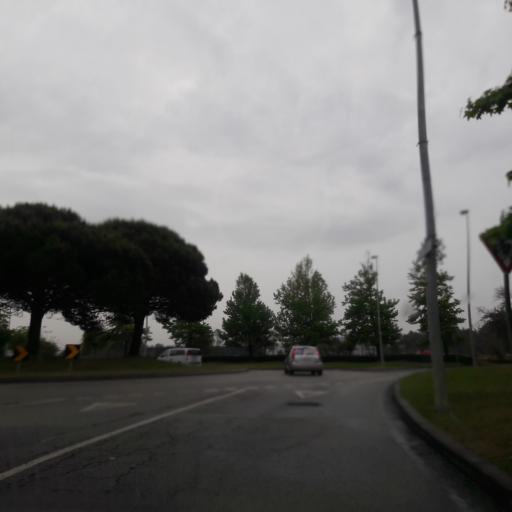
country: PT
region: Porto
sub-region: Vila do Conde
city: Arvore
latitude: 41.3301
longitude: -8.7190
